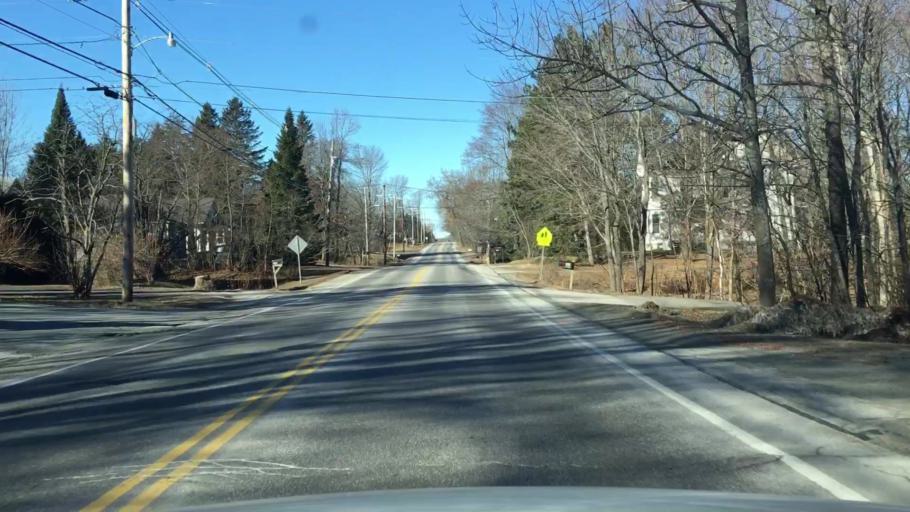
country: US
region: Maine
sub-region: Penobscot County
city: Bangor
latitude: 44.8156
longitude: -68.7982
